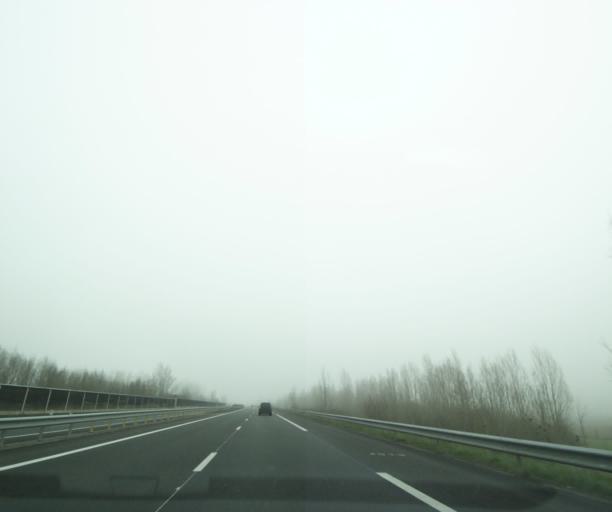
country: FR
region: Midi-Pyrenees
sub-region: Departement du Tarn-et-Garonne
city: Realville
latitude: 44.1188
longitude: 1.4745
